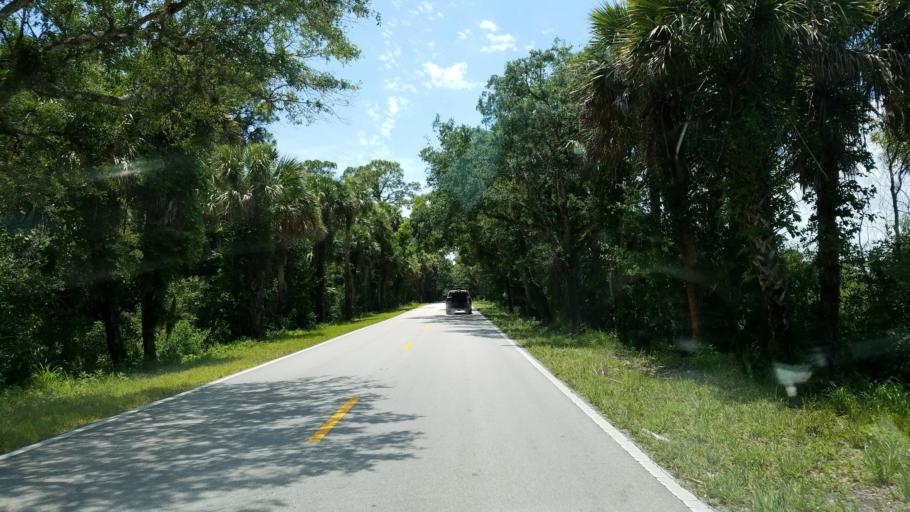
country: US
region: Florida
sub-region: Martin County
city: Indiantown
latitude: 27.1621
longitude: -80.6083
